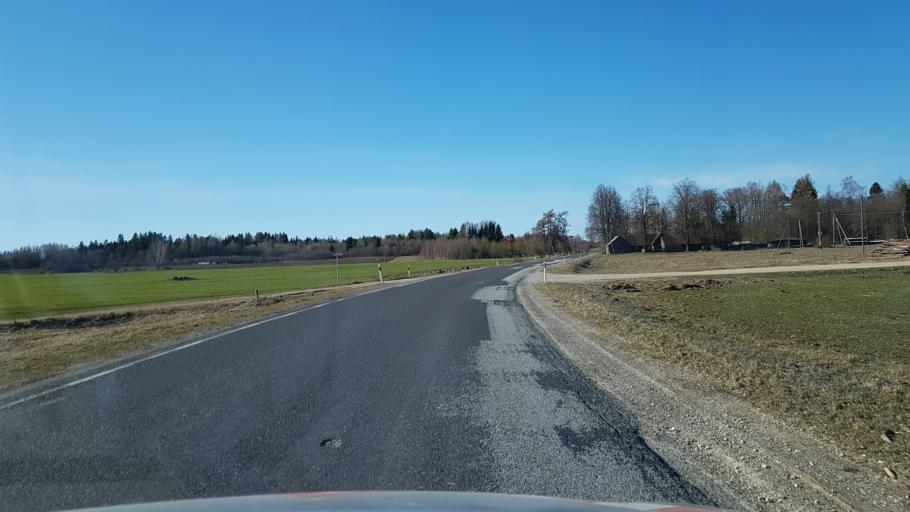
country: EE
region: Laeaene-Virumaa
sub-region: Vinni vald
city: Vinni
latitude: 59.3022
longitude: 26.5346
